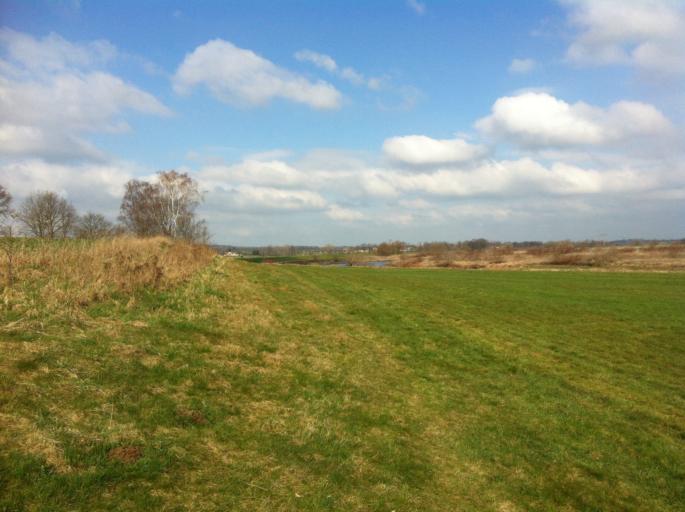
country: DE
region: Saxony
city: Trebsen
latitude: 51.3087
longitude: 12.7518
